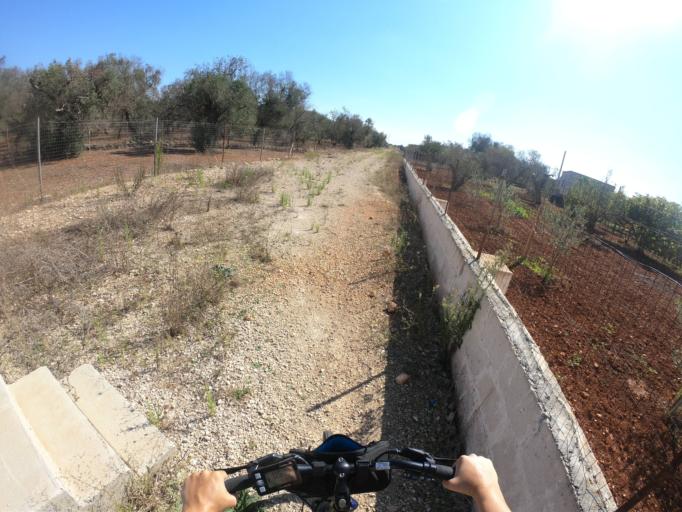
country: IT
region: Apulia
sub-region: Provincia di Lecce
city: Galatone
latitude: 40.1319
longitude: 18.0683
